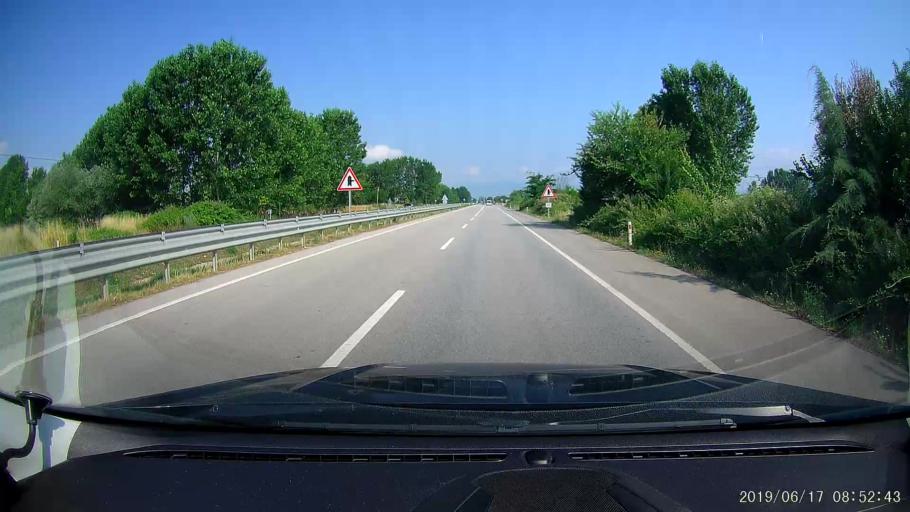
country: TR
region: Tokat
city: Erbaa
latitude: 40.7015
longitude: 36.4922
